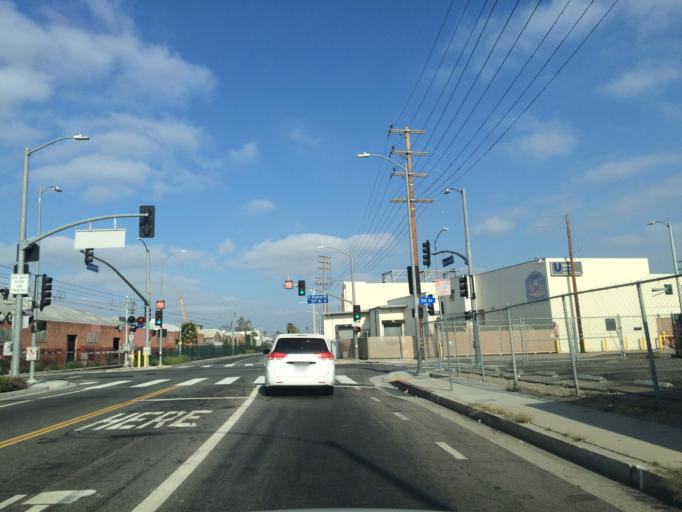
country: US
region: California
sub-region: Los Angeles County
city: View Park-Windsor Hills
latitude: 34.0215
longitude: -118.3290
